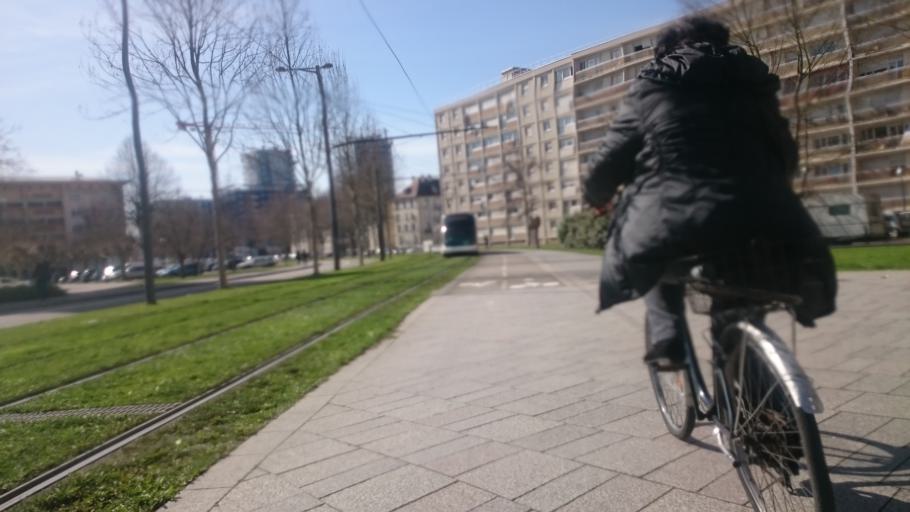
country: FR
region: Alsace
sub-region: Departement du Bas-Rhin
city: Strasbourg
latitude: 48.5764
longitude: 7.7682
